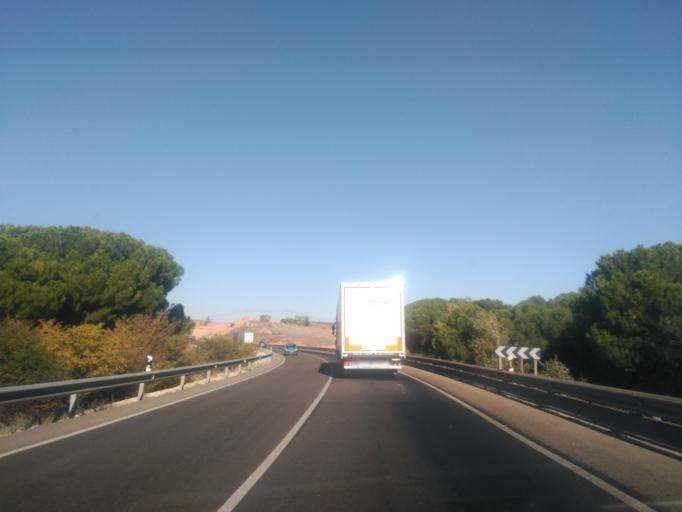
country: ES
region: Castille and Leon
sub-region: Provincia de Valladolid
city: Penafiel
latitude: 41.6069
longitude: -4.1414
